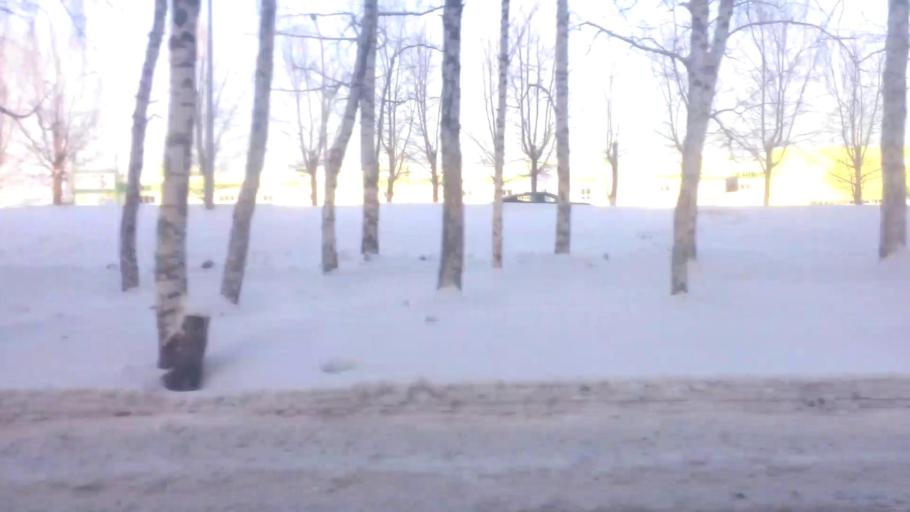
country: RU
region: Altai Krai
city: Novosilikatnyy
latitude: 53.3458
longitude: 83.6540
